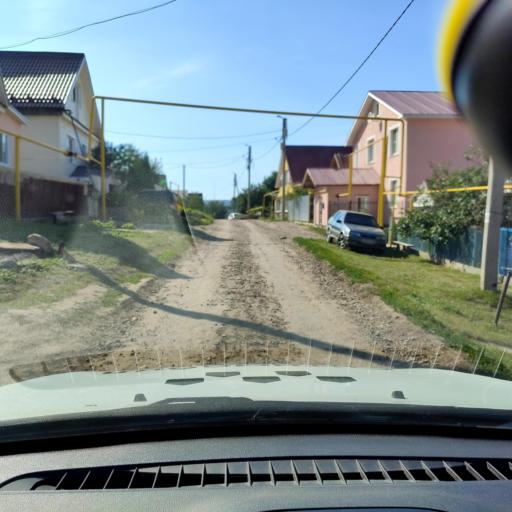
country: RU
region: Samara
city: Zhigulevsk
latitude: 53.3980
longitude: 49.5272
